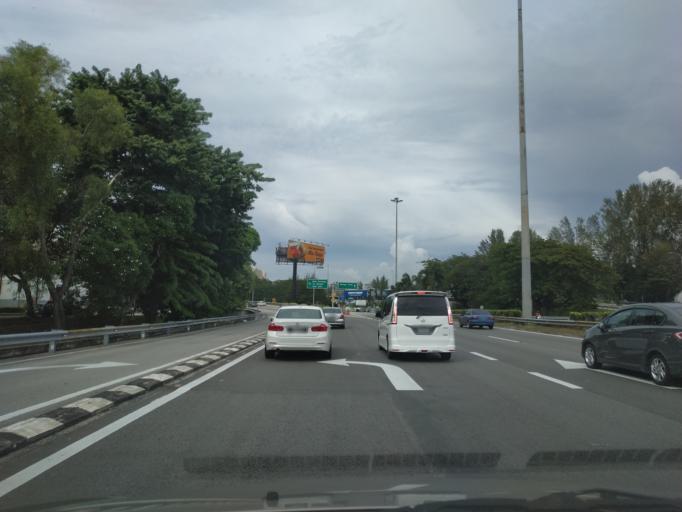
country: MY
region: Penang
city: George Town
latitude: 5.3770
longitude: 100.3163
